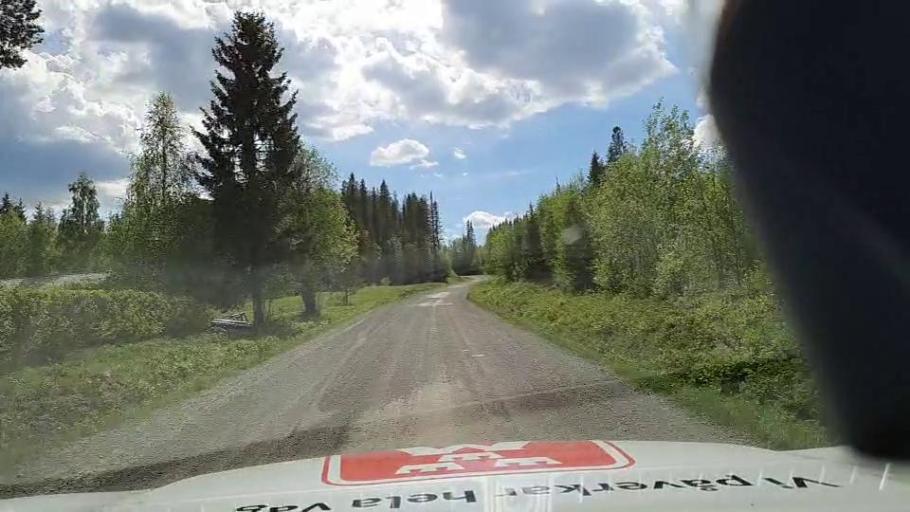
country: SE
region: Vaesterbotten
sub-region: Vilhelmina Kommun
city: Sjoberg
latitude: 64.5649
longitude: 15.8507
